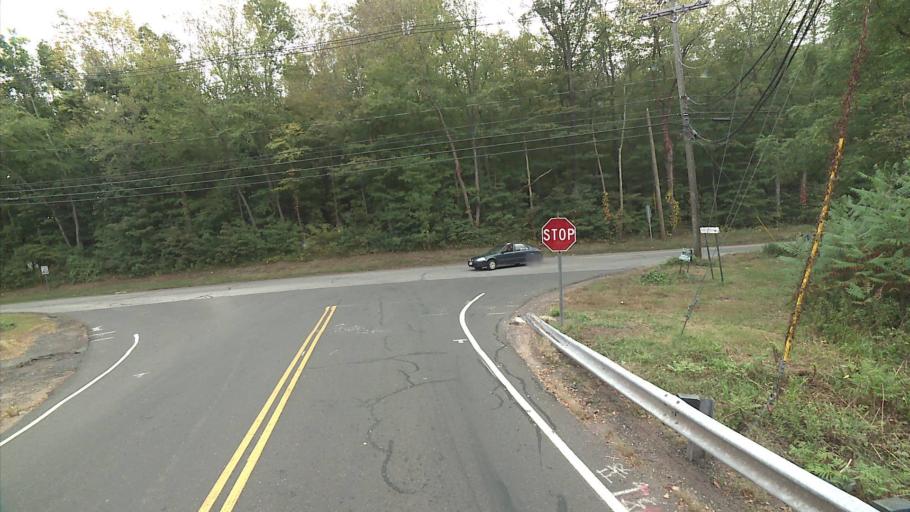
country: US
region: Connecticut
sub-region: Middlesex County
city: Durham
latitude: 41.4749
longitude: -72.7274
